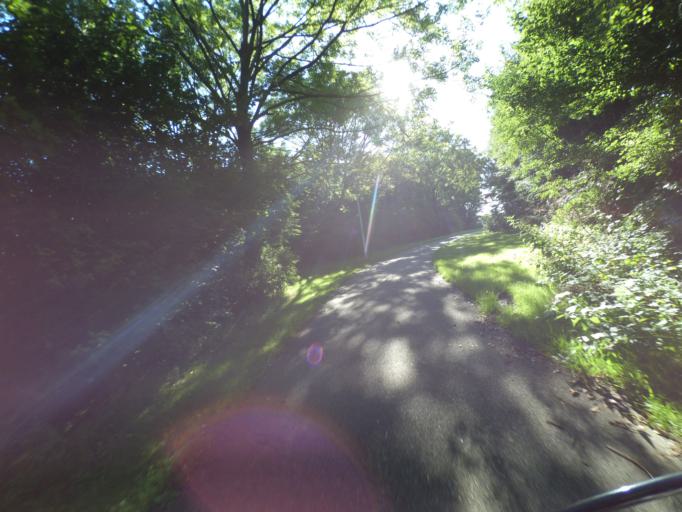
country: NL
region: Friesland
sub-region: Gemeente Achtkarspelen
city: Buitenpost
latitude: 53.2616
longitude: 6.1431
